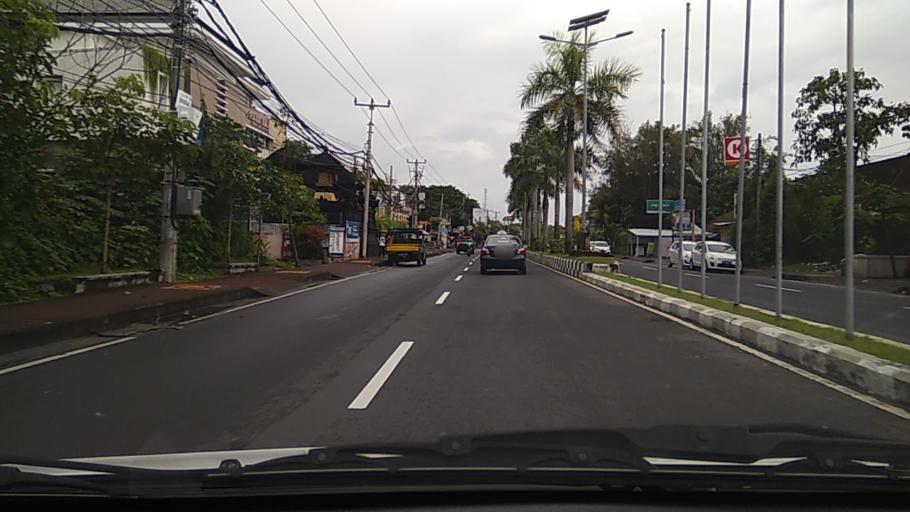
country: ID
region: Bali
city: Bualu
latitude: -8.7976
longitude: 115.2212
